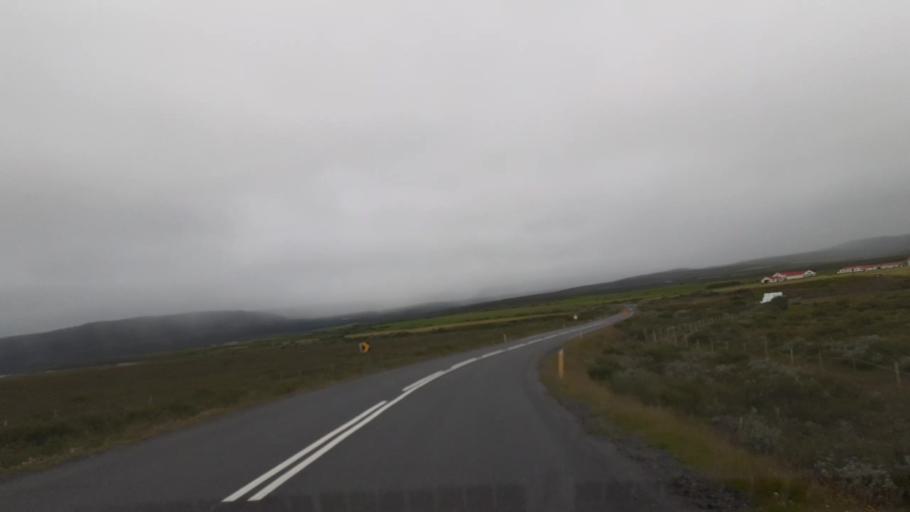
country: IS
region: Northeast
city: Husavik
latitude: 66.1082
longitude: -16.4434
